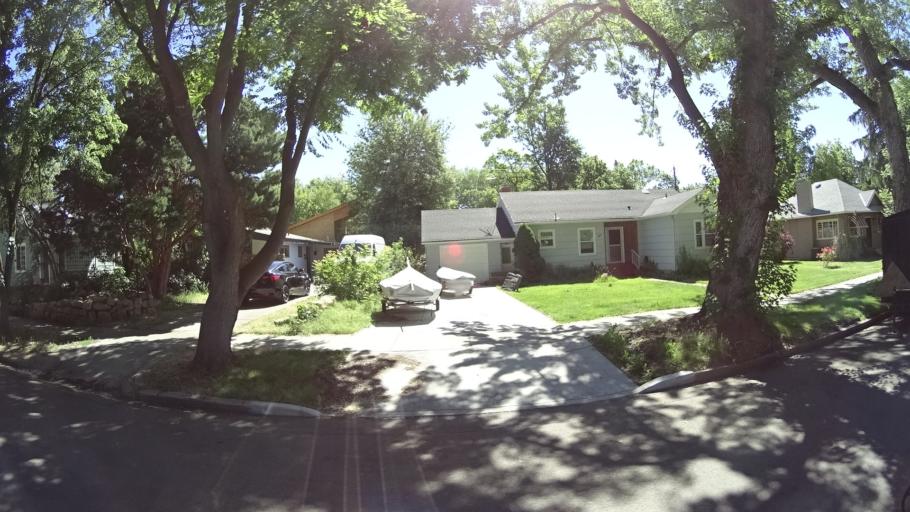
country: US
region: Idaho
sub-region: Ada County
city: Boise
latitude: 43.6376
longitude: -116.2134
